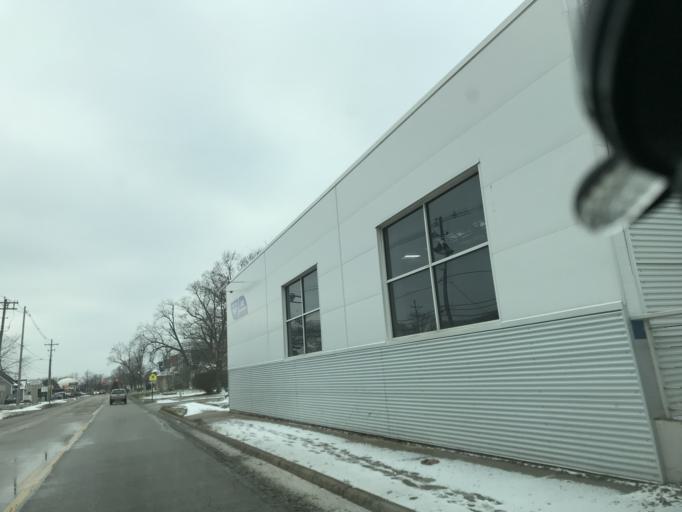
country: US
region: Michigan
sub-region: Ottawa County
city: Zeeland
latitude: 42.8139
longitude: -86.0253
